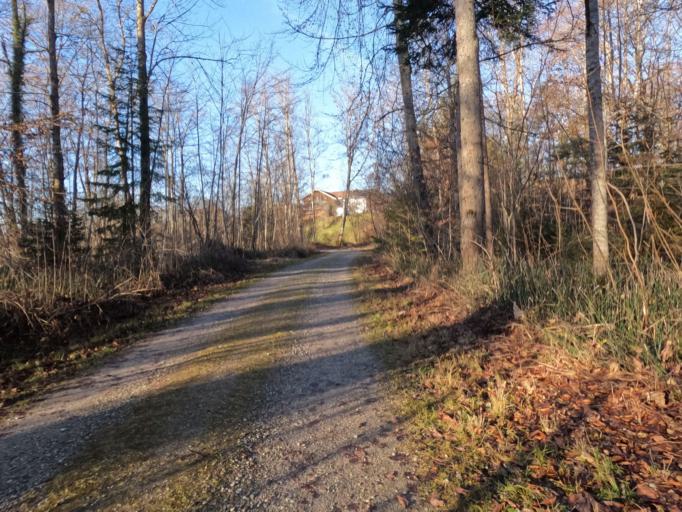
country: DE
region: Bavaria
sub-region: Upper Bavaria
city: Traunstein
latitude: 47.8956
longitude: 12.6333
